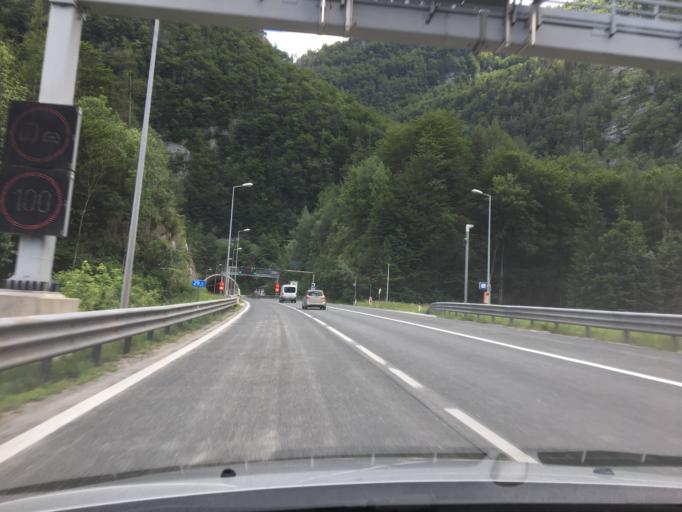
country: AT
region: Salzburg
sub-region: Politischer Bezirk Hallein
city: Golling an der Salzach
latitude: 47.5784
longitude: 13.1608
